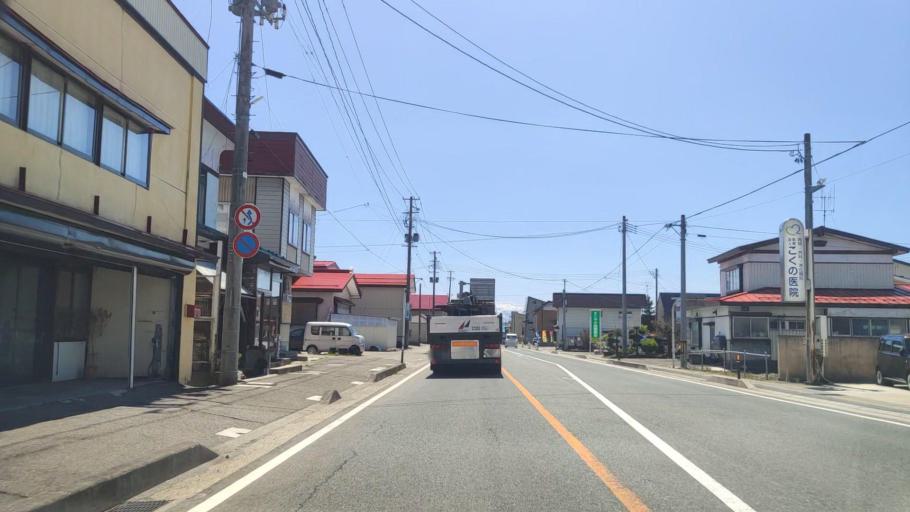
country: JP
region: Yamagata
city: Shinjo
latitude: 38.8106
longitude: 140.3231
